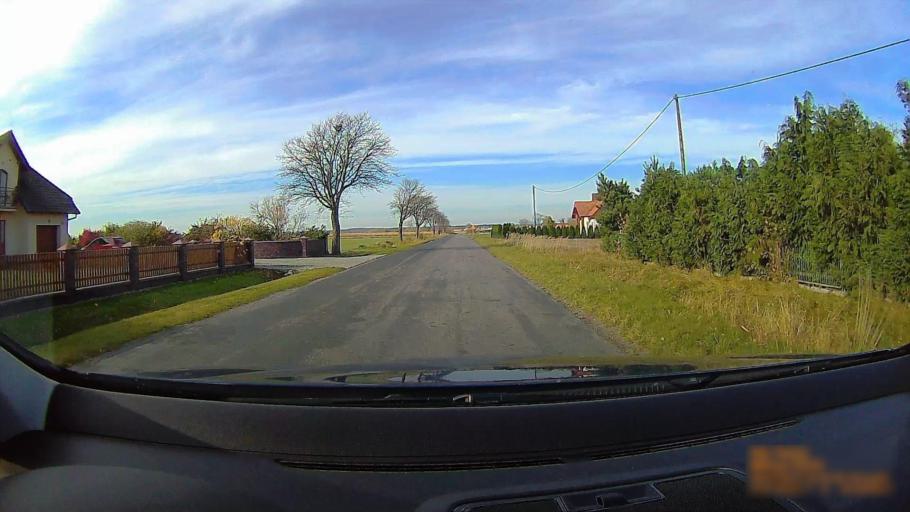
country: PL
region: Greater Poland Voivodeship
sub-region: Powiat ostrzeszowski
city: Doruchow
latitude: 51.4236
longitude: 18.0581
